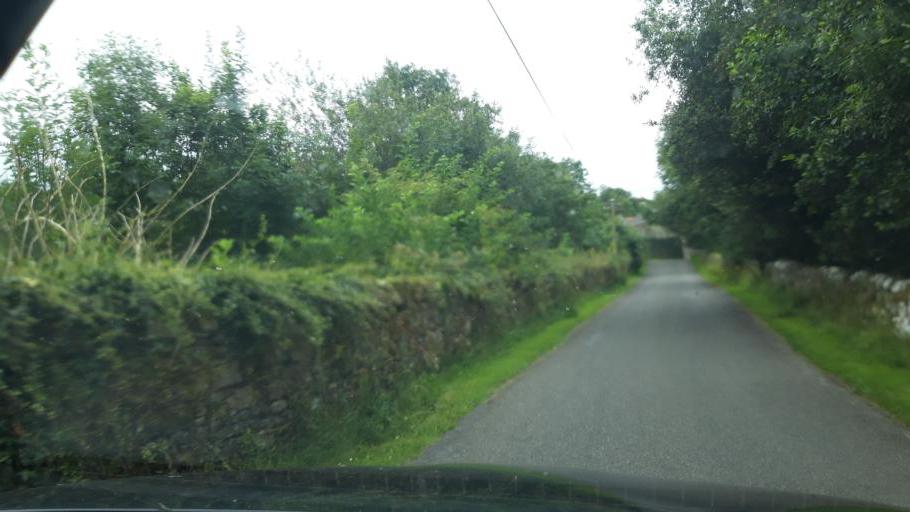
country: IE
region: Leinster
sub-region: Kilkenny
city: Thomastown
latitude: 52.6274
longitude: -7.0659
